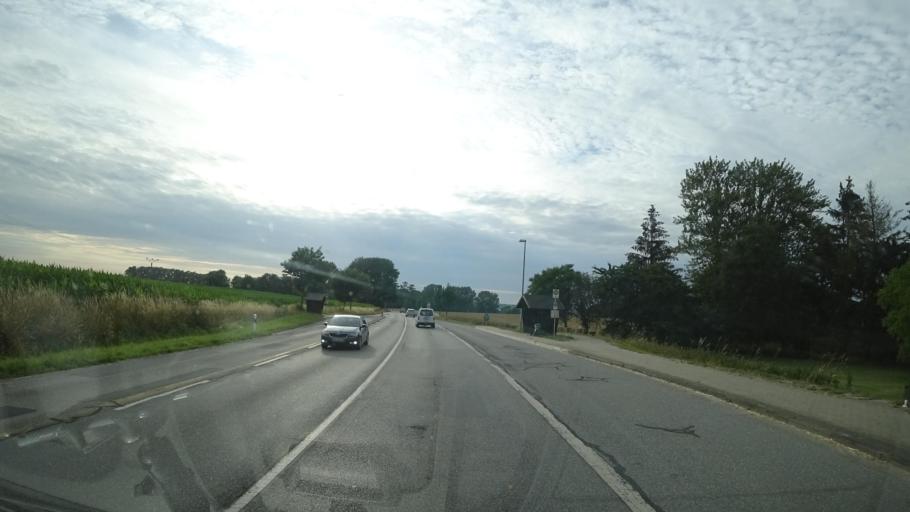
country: DE
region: Mecklenburg-Vorpommern
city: Putbus
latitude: 54.4036
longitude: 13.5028
